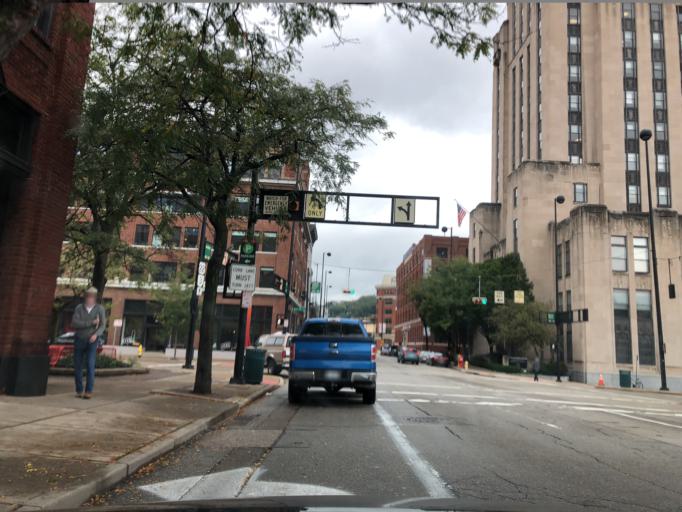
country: US
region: Kentucky
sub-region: Campbell County
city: Newport
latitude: 39.1050
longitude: -84.5072
